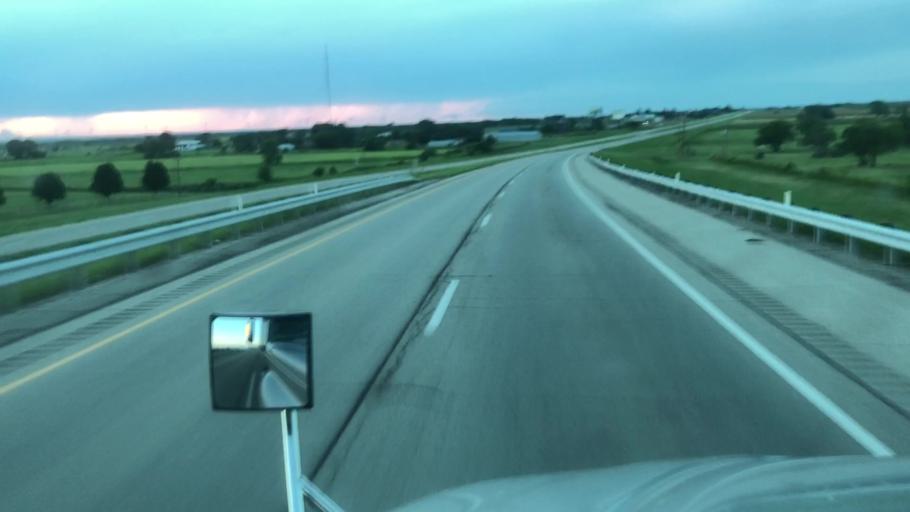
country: US
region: Oklahoma
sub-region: Kay County
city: Ponca City
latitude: 36.7766
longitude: -97.0664
